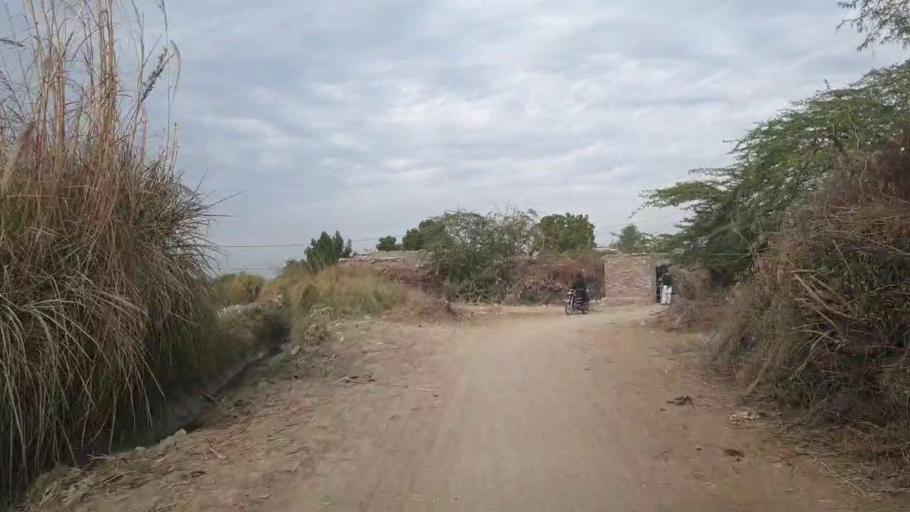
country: PK
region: Sindh
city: Sinjhoro
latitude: 26.0261
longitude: 68.8737
